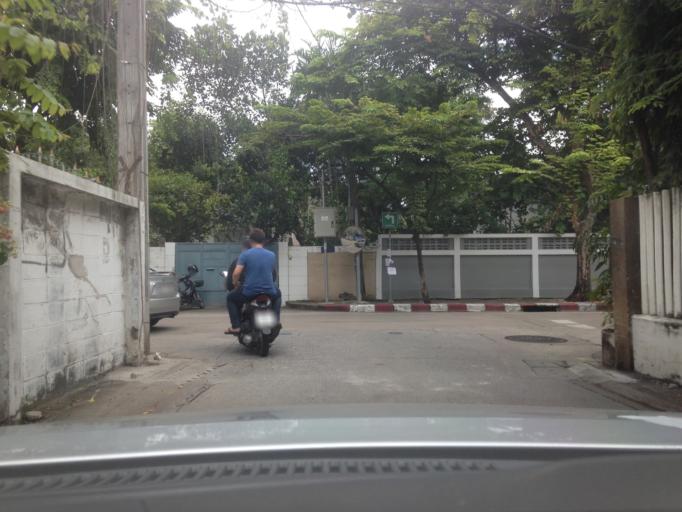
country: TH
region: Bangkok
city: Phaya Thai
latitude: 13.7866
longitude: 100.5442
